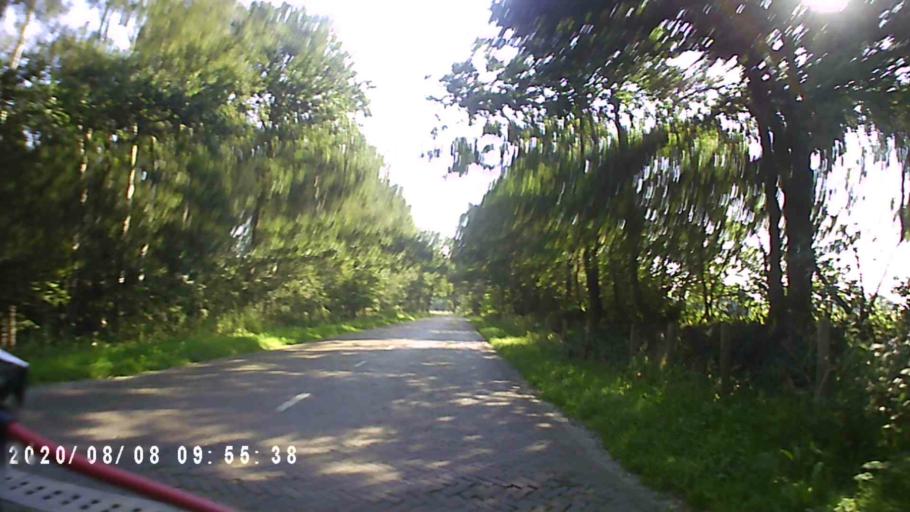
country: NL
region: Groningen
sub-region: Gemeente Leek
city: Leek
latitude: 53.0941
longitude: 6.4006
